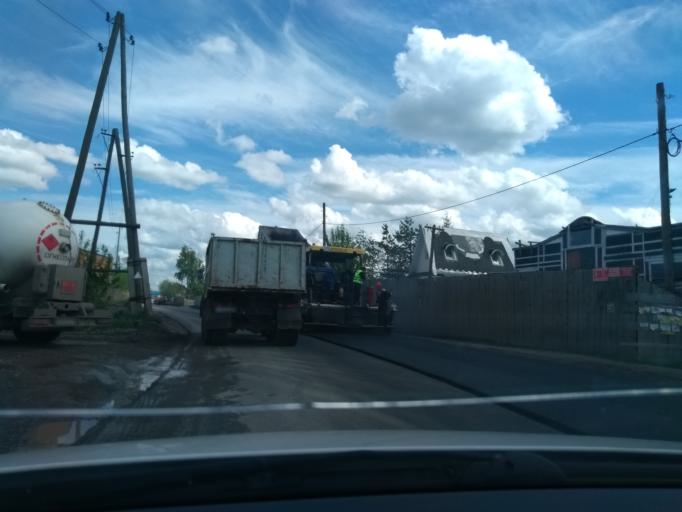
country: RU
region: Perm
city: Kondratovo
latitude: 58.0128
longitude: 56.0577
